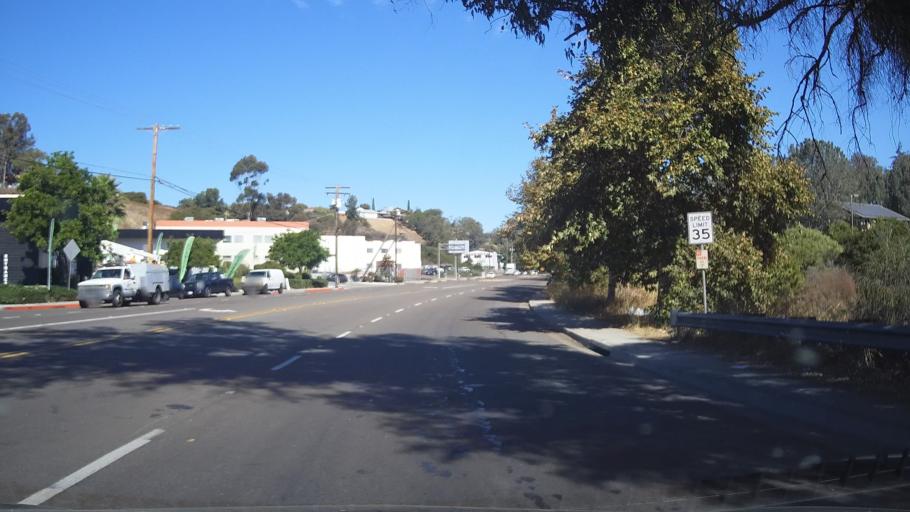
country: US
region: California
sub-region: San Diego County
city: National City
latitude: 32.7197
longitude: -117.1102
